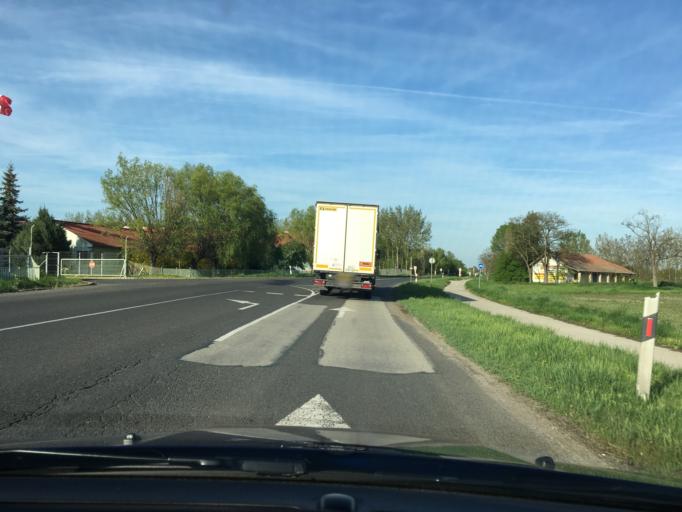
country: HU
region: Bekes
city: Szeghalom
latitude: 47.0099
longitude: 21.1338
